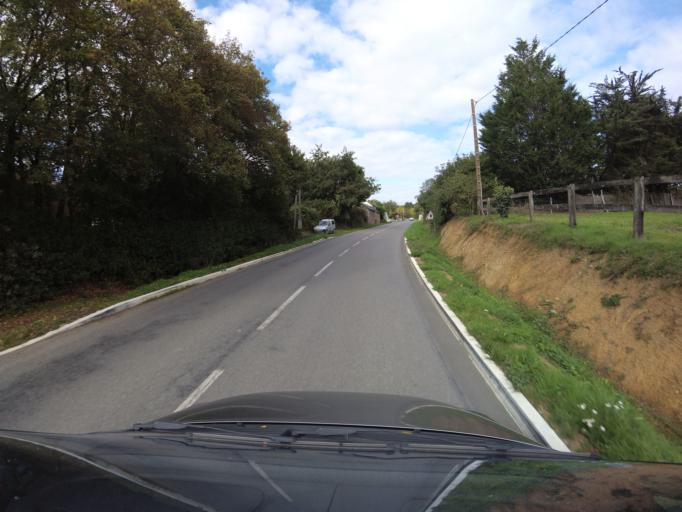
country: FR
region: Pays de la Loire
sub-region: Departement de la Loire-Atlantique
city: Bouvron
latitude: 47.4750
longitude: -1.8400
